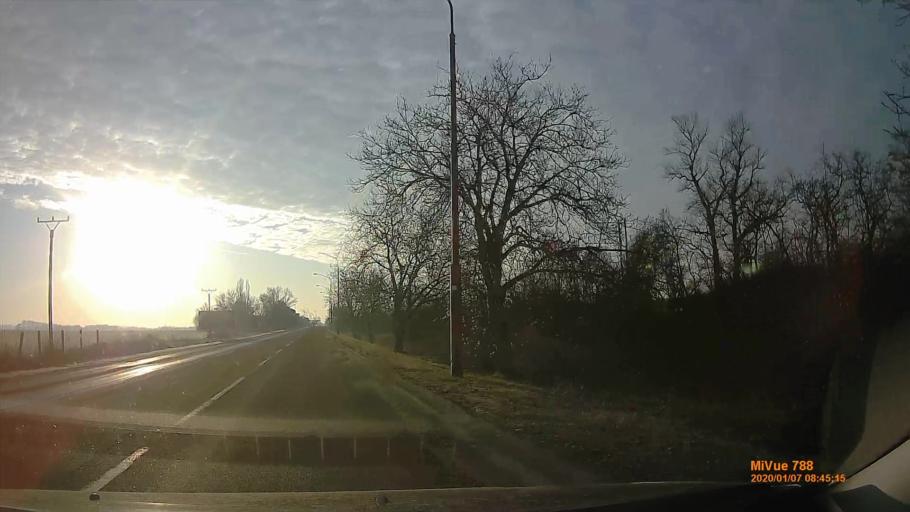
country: HU
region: Gyor-Moson-Sopron
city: Rajka
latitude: 48.0187
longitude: 17.1760
